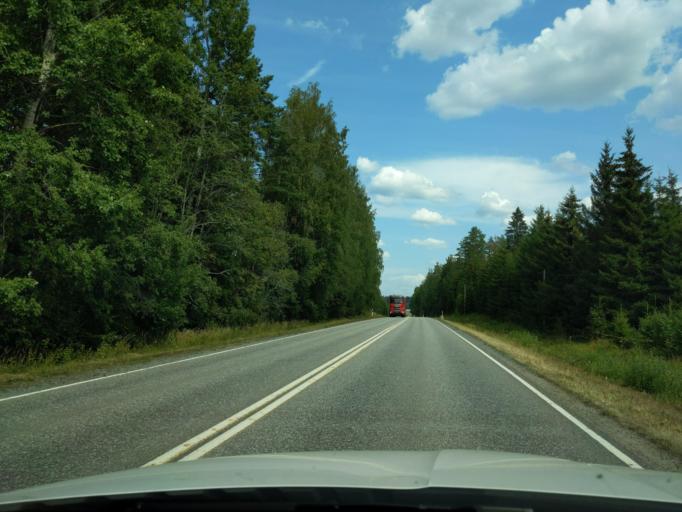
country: FI
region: Haeme
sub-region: Haemeenlinna
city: Lammi
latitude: 61.1193
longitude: 24.9385
